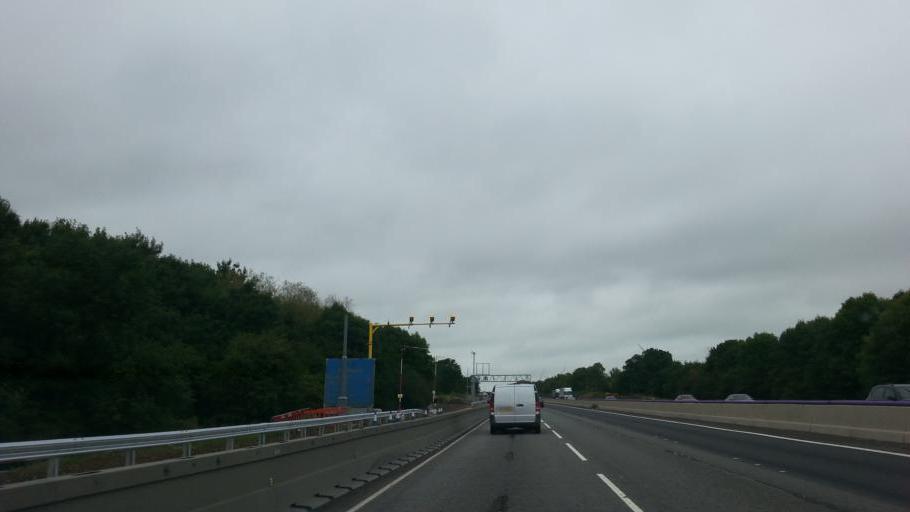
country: GB
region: England
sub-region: Northamptonshire
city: Long Buckby
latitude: 52.3581
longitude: -1.1563
